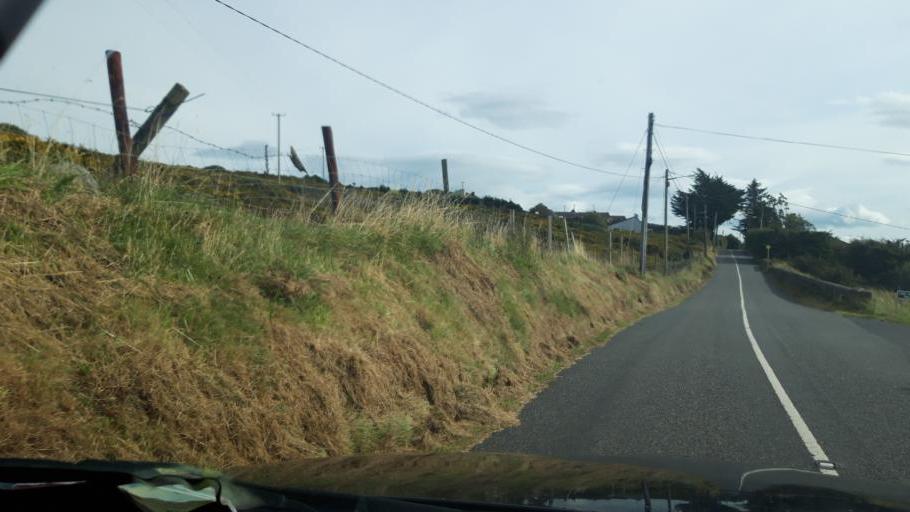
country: IE
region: Leinster
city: Balally
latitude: 53.2222
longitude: -6.2364
